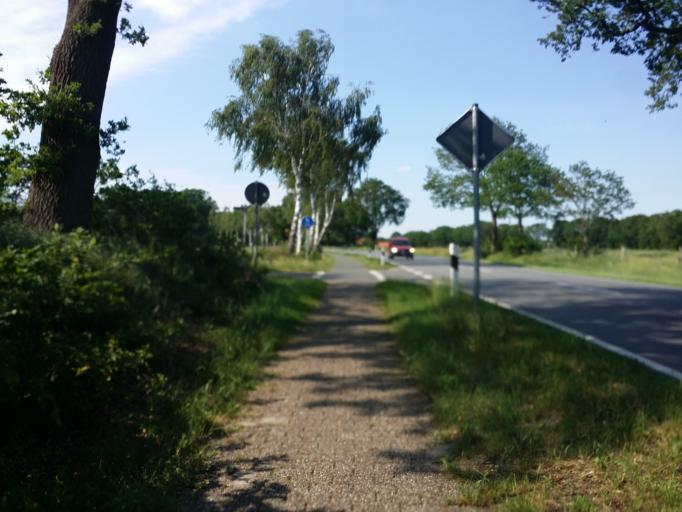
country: DE
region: Lower Saxony
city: Wiefelstede
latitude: 53.2749
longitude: 8.1108
